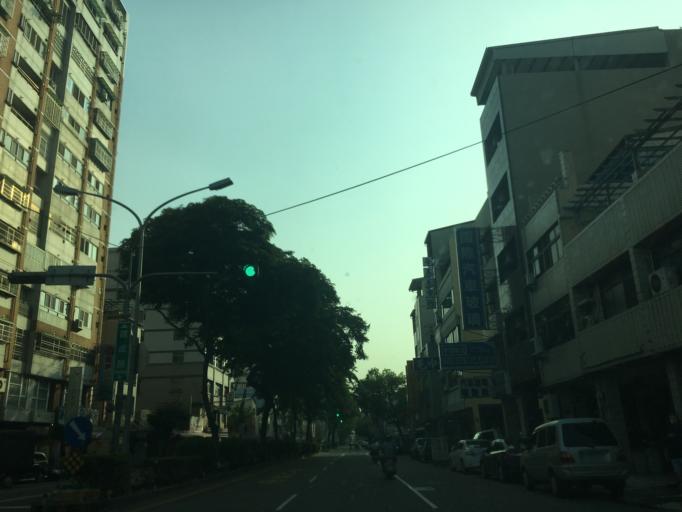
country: TW
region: Taiwan
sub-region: Taichung City
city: Taichung
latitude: 24.1289
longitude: 120.6832
